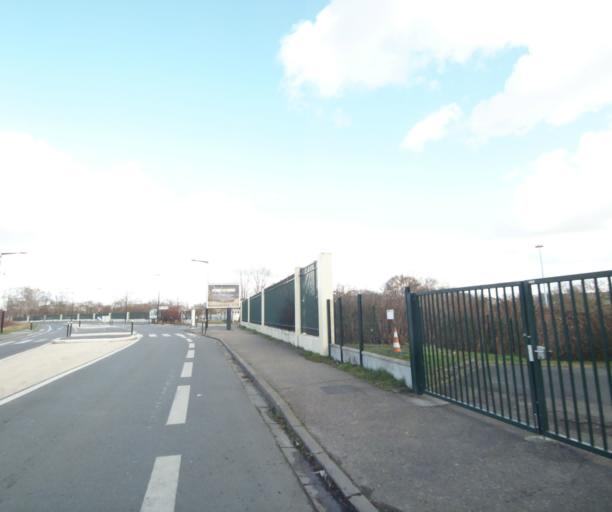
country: FR
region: Ile-de-France
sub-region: Departement de Seine-Saint-Denis
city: Villetaneuse
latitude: 48.9544
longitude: 2.3386
